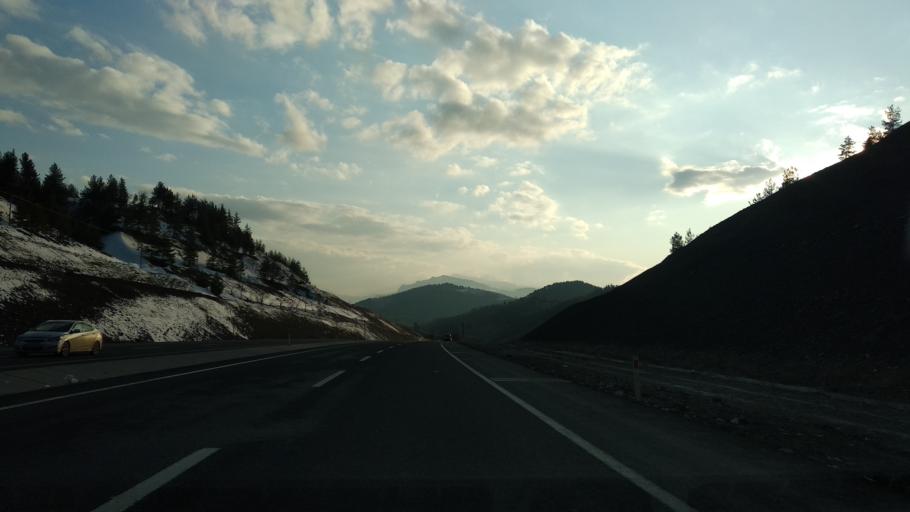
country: TR
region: Kahramanmaras
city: Yenicekale
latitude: 37.7146
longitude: 36.6947
